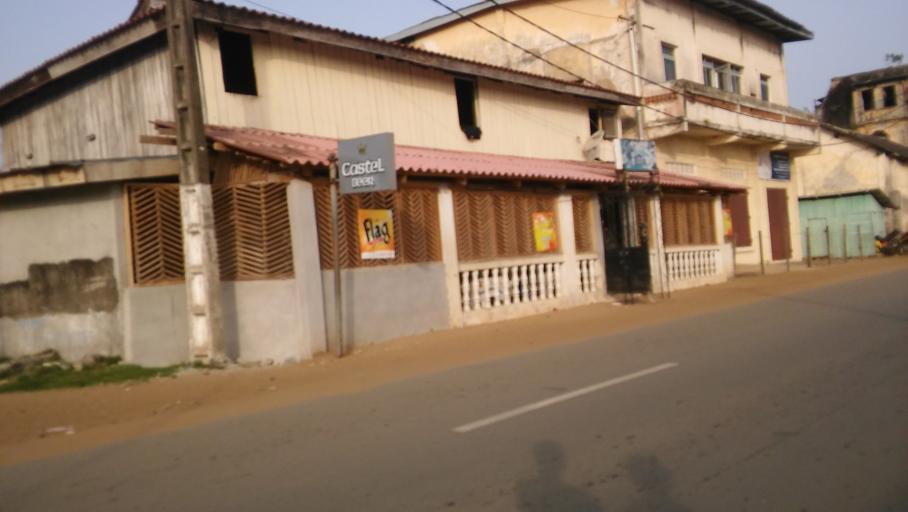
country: CI
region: Sud-Comoe
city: Grand-Bassam
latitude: 5.1957
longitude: -3.7289
